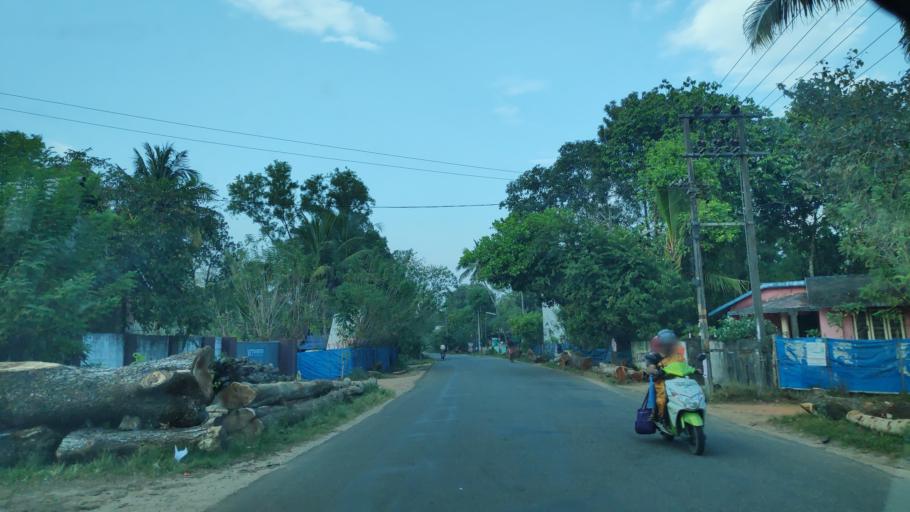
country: IN
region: Kerala
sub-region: Alappuzha
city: Shertallai
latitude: 9.6365
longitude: 76.3717
